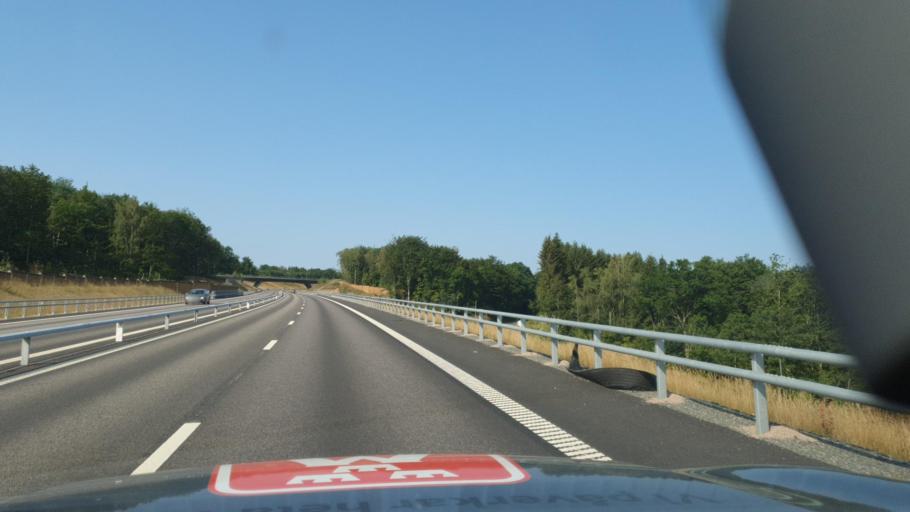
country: SE
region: Skane
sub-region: Hassleholms Kommun
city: Vinslov
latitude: 55.9491
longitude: 13.8980
